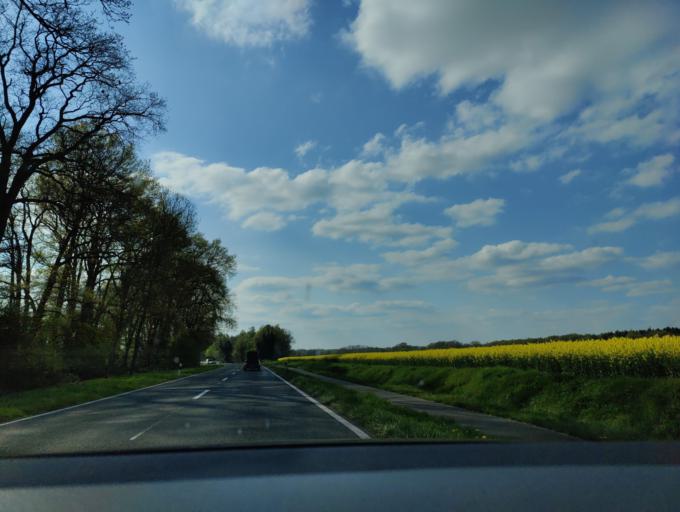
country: DE
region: Lower Saxony
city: Engden
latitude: 52.3735
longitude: 7.2237
